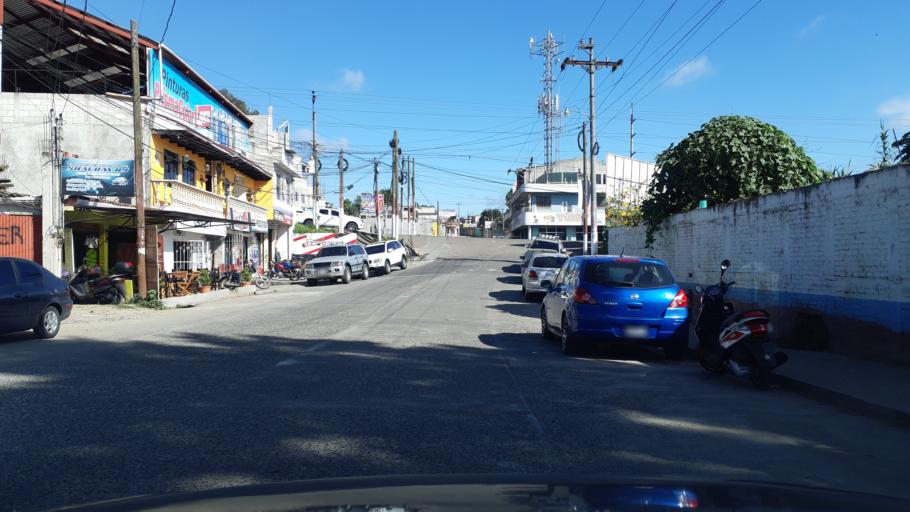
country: GT
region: Chimaltenango
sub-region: Municipio de Chimaltenango
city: Chimaltenango
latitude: 14.6583
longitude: -90.8218
